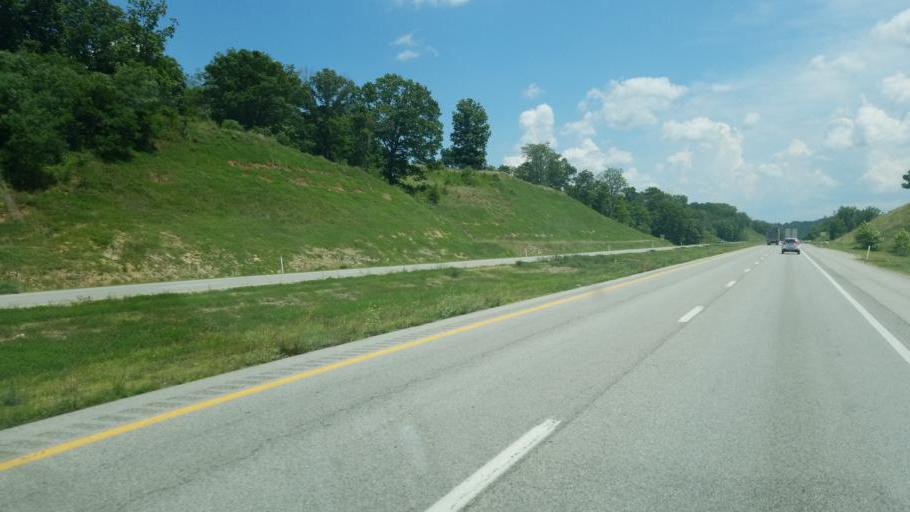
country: US
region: West Virginia
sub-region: Mason County
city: Point Pleasant
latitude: 38.7868
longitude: -82.0856
